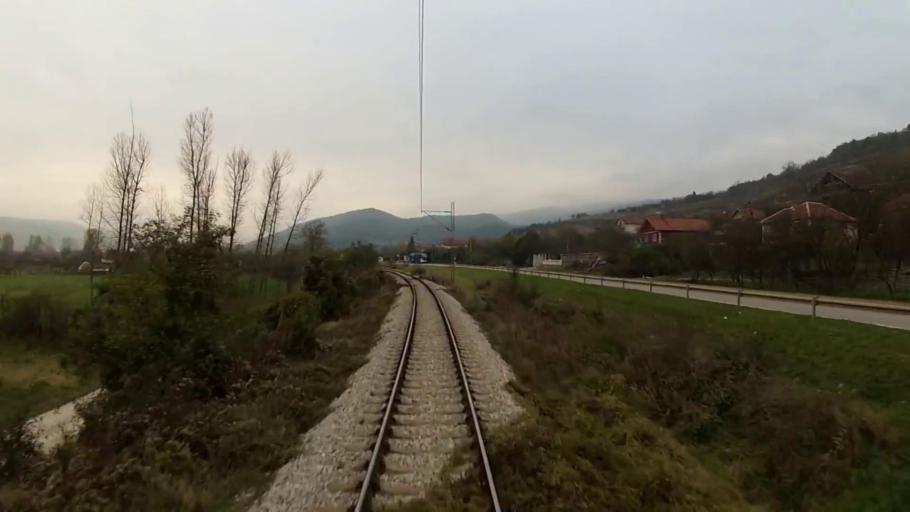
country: RS
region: Central Serbia
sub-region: Pirotski Okrug
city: Dimitrovgrad
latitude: 43.0053
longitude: 22.8077
